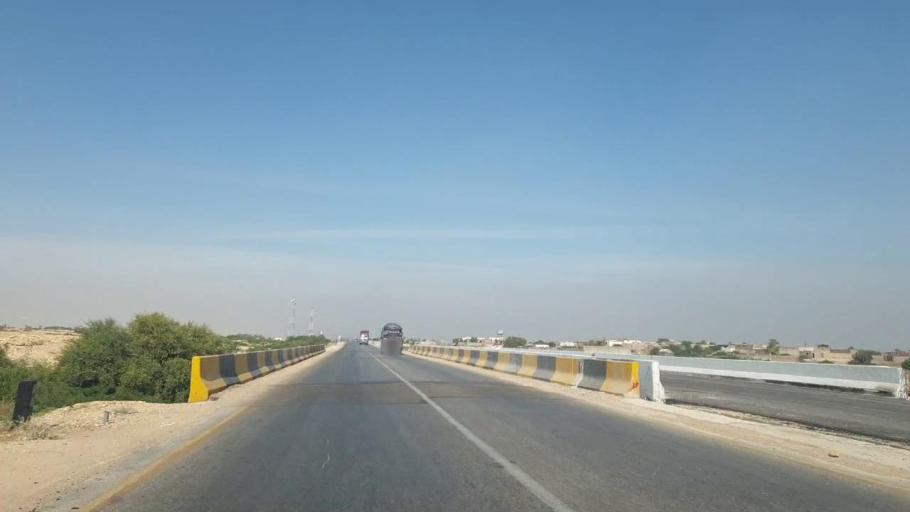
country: PK
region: Sindh
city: Hala
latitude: 25.6956
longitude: 68.2955
